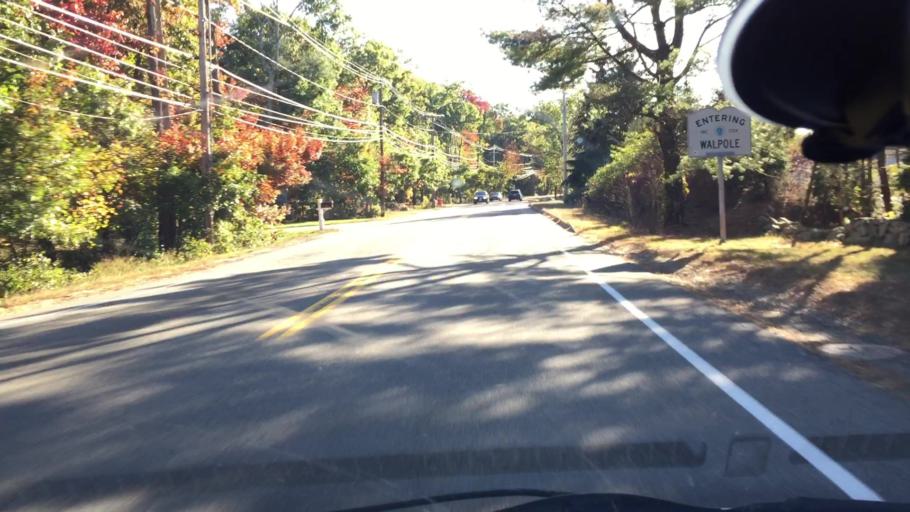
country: US
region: Massachusetts
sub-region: Norfolk County
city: Westwood
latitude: 42.2041
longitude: -71.2589
